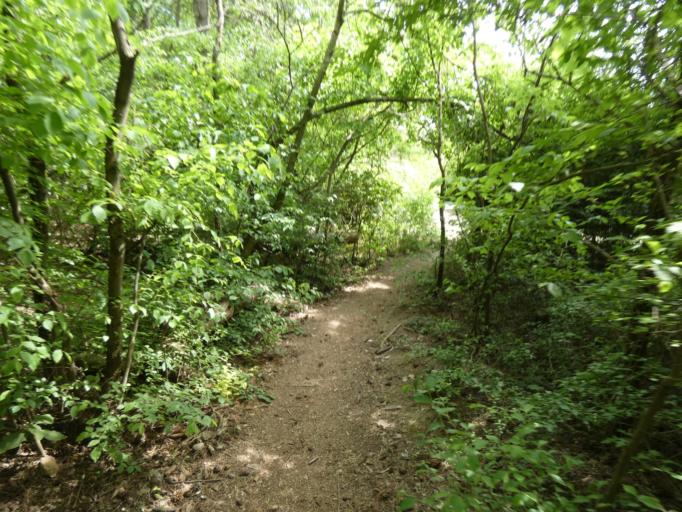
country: HU
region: Pest
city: Pilisborosjeno
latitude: 47.6116
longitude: 18.9983
